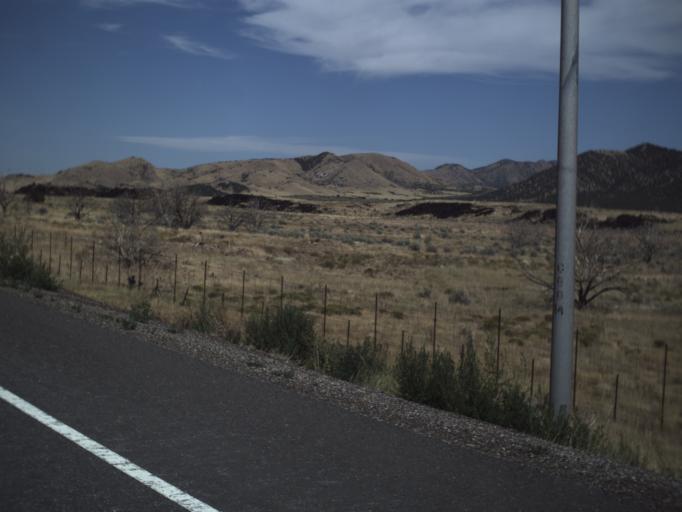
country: US
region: Utah
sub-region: Beaver County
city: Beaver
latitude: 38.5804
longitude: -112.6034
